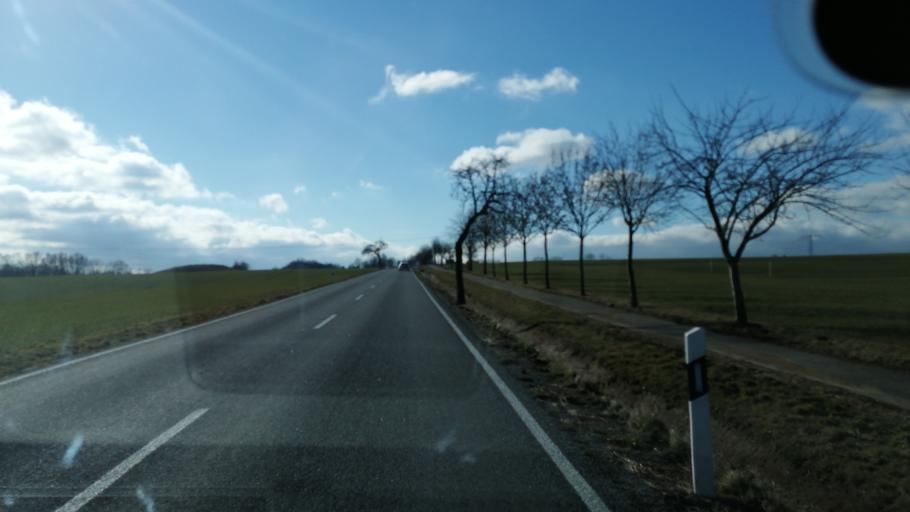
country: DE
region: Saxony
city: Lobau
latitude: 51.1422
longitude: 14.7049
